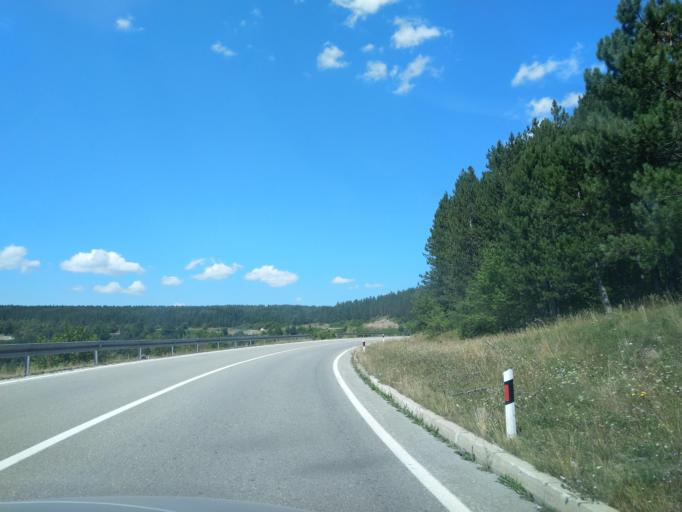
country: RS
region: Central Serbia
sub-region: Zlatiborski Okrug
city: Sjenica
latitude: 43.3020
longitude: 19.9300
